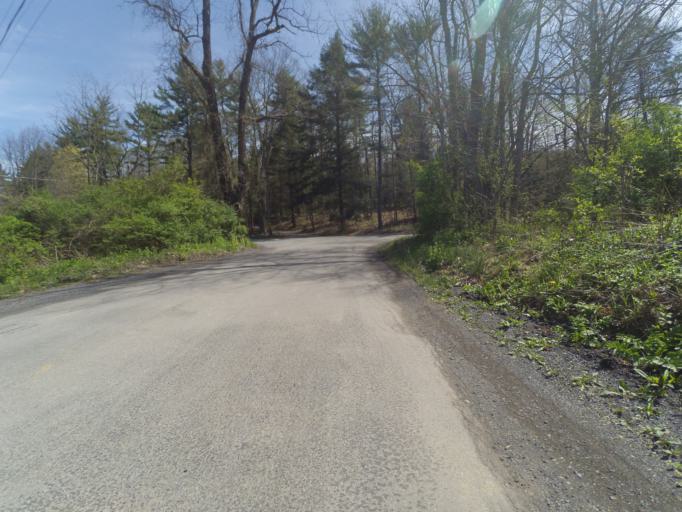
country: US
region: Pennsylvania
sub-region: Blair County
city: Tyrone
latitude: 40.6013
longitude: -78.2133
